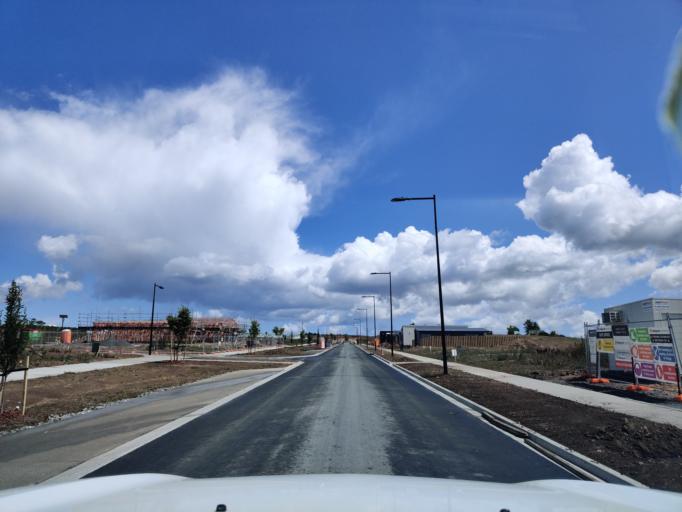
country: NZ
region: Waikato
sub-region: Waikato District
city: Te Kauwhata
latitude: -37.4127
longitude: 175.1507
